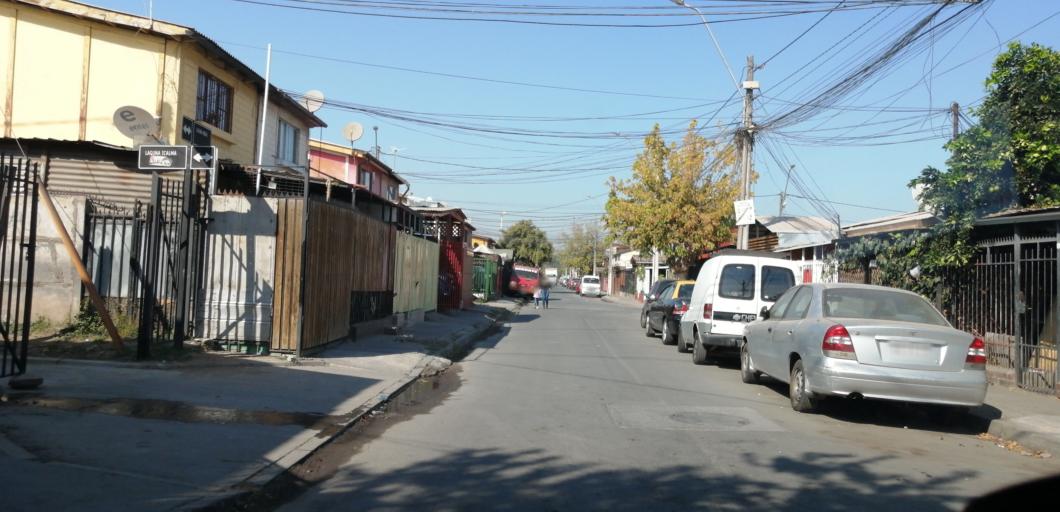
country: CL
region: Santiago Metropolitan
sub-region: Provincia de Santiago
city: Lo Prado
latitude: -33.4622
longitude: -70.7473
